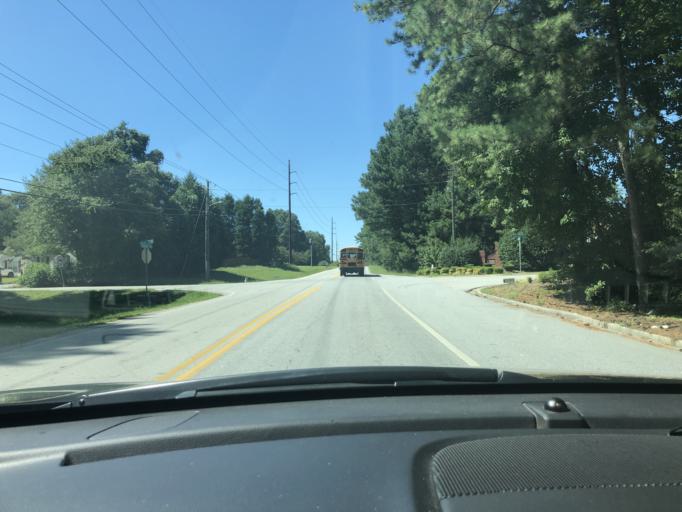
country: US
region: Georgia
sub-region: Gwinnett County
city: Grayson
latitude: 33.9135
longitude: -83.9346
